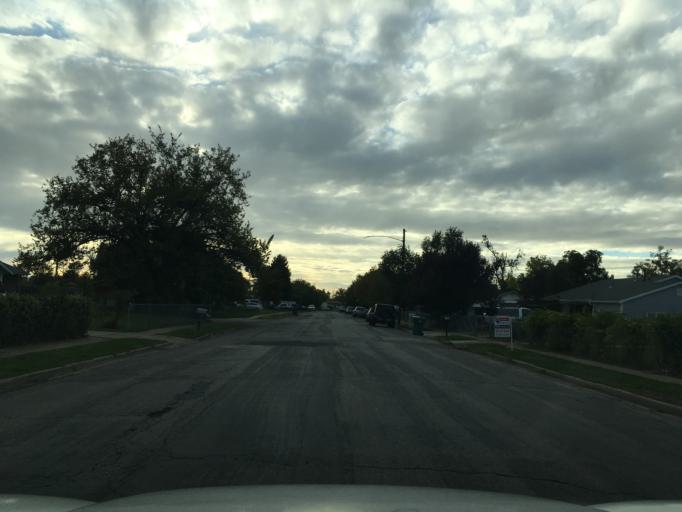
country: US
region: Utah
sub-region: Davis County
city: Layton
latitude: 41.0815
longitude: -111.9951
